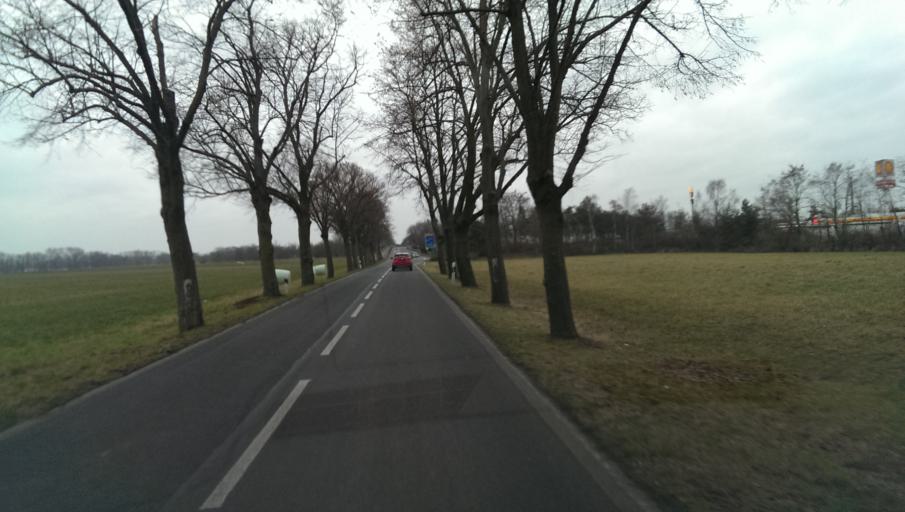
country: DE
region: Brandenburg
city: Grossbeeren
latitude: 52.3102
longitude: 13.3156
